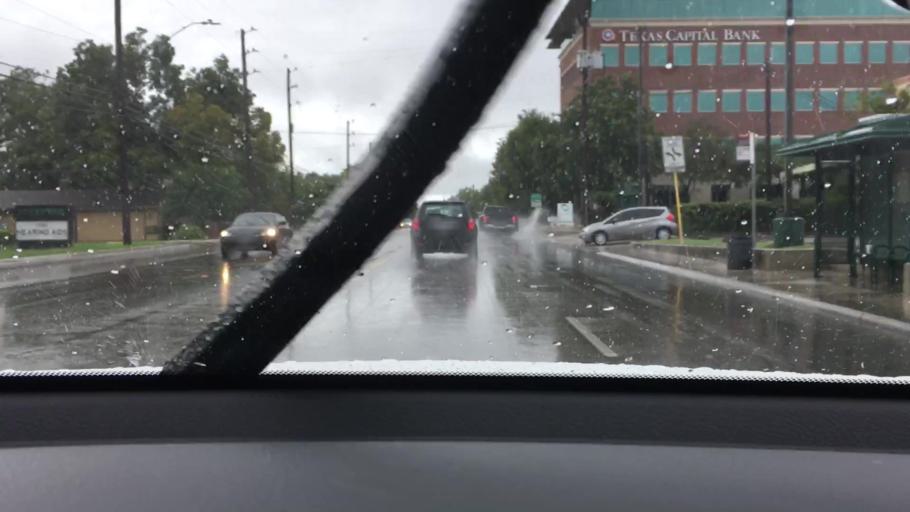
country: US
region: Texas
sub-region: Bexar County
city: Alamo Heights
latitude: 29.4967
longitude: -98.4666
